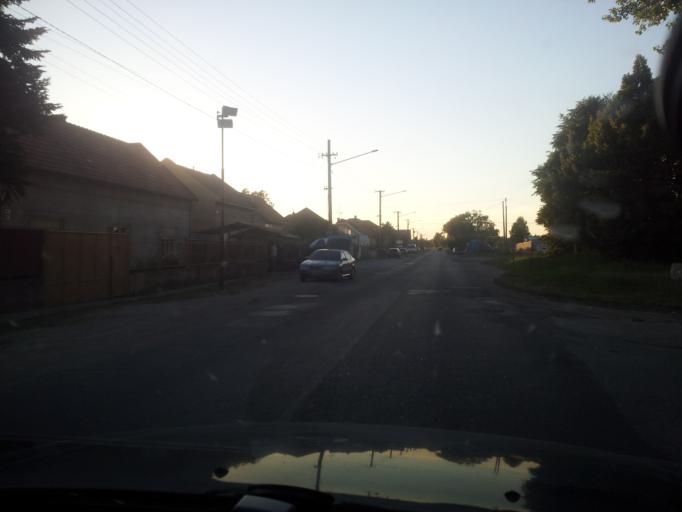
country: SK
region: Nitriansky
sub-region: Okres Nove Zamky
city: Sturovo
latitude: 47.8037
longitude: 18.7104
